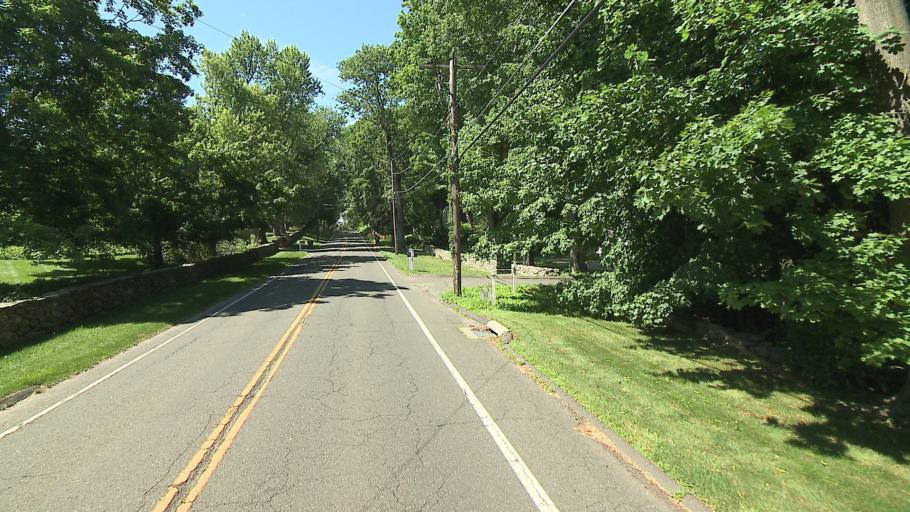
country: US
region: Connecticut
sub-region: Fairfield County
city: Ridgefield
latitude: 41.2623
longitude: -73.5121
